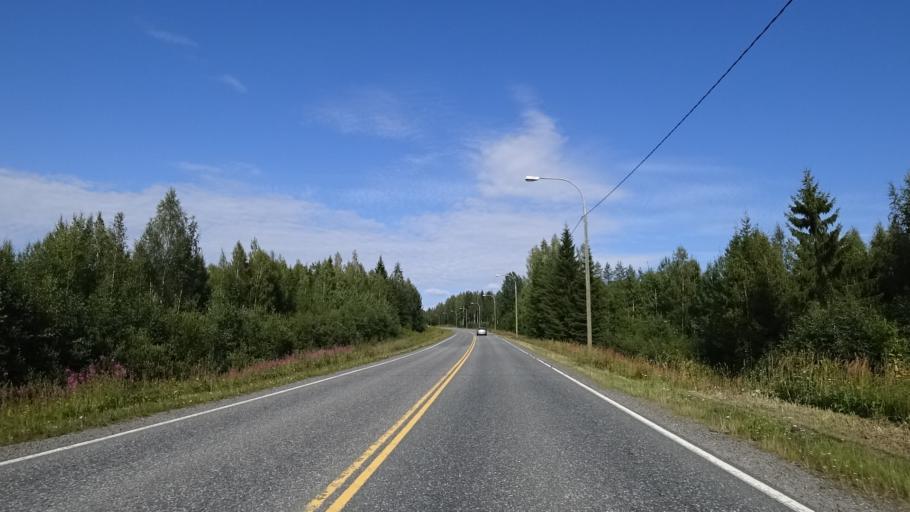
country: FI
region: North Karelia
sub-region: Joensuu
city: Eno
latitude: 62.7795
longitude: 30.0696
